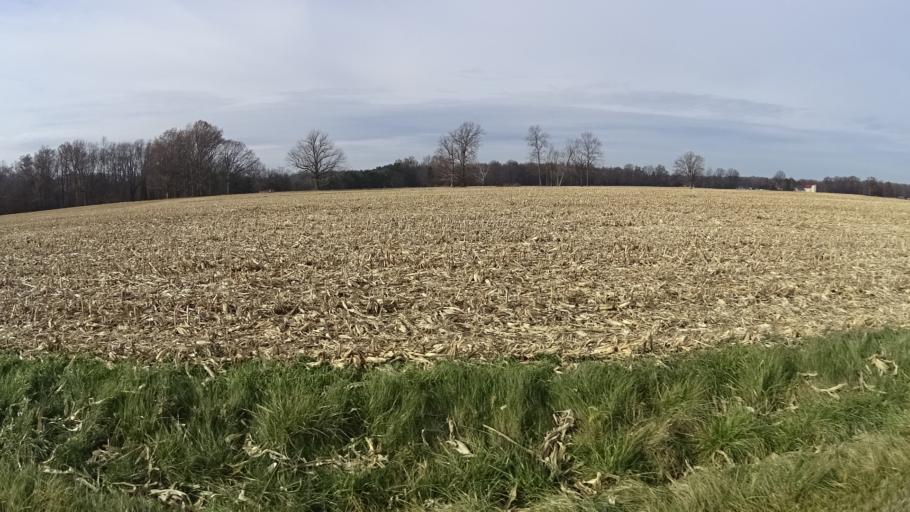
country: US
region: Ohio
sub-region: Lorain County
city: Grafton
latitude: 41.2339
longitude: -82.0033
